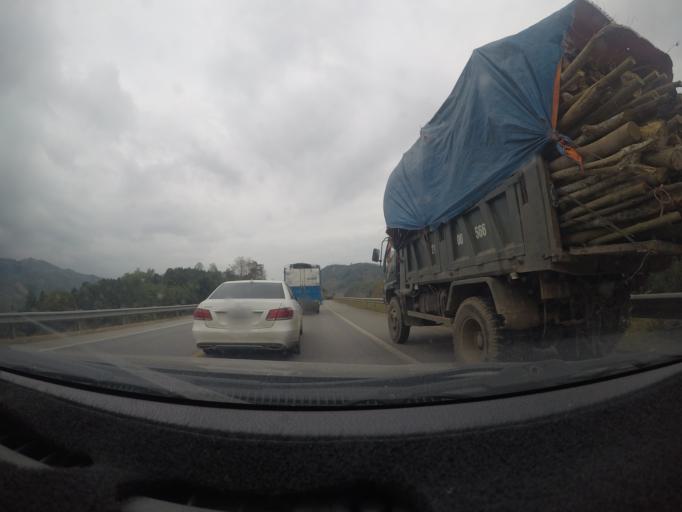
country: VN
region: Lao Cai
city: Thi Tran Pho Rang
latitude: 22.1393
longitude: 104.3838
